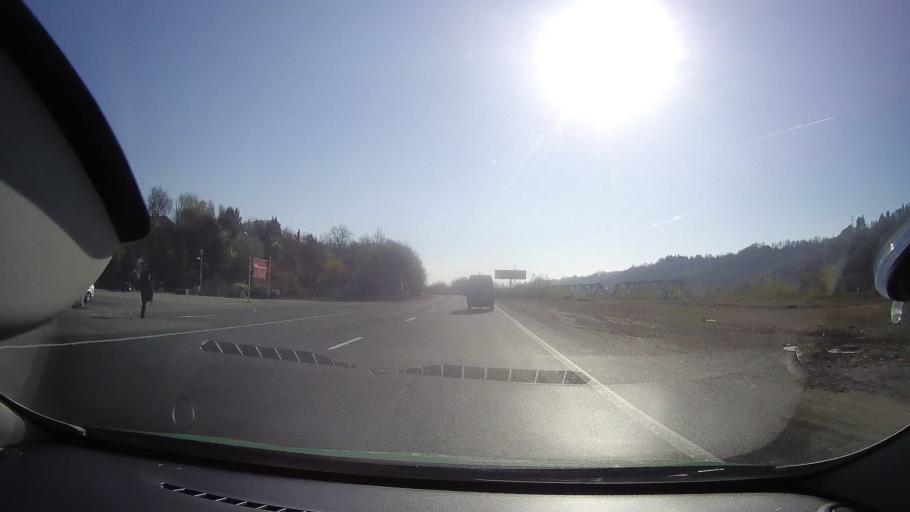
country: RO
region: Prahova
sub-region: Oras Breaza
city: Breaza de Sus
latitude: 45.2061
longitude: 25.6604
